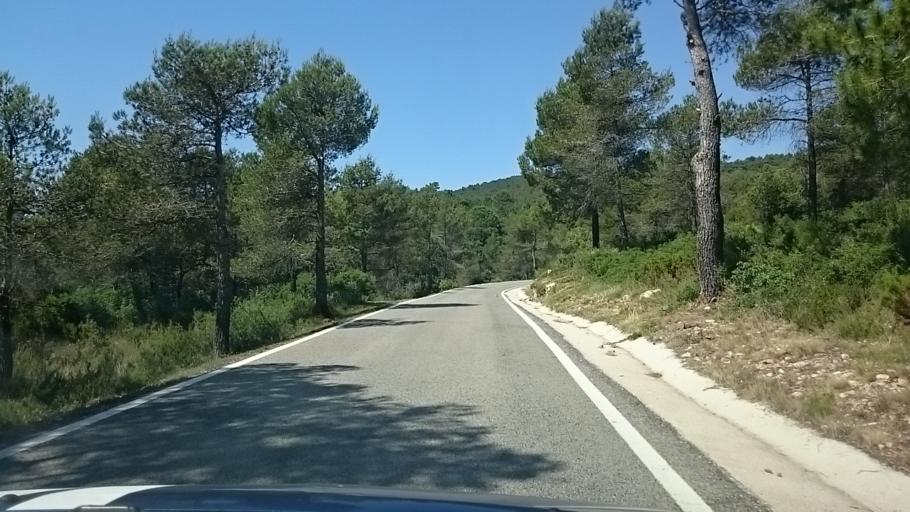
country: ES
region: Catalonia
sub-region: Provincia de Tarragona
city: Querol
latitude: 41.3954
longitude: 1.4366
